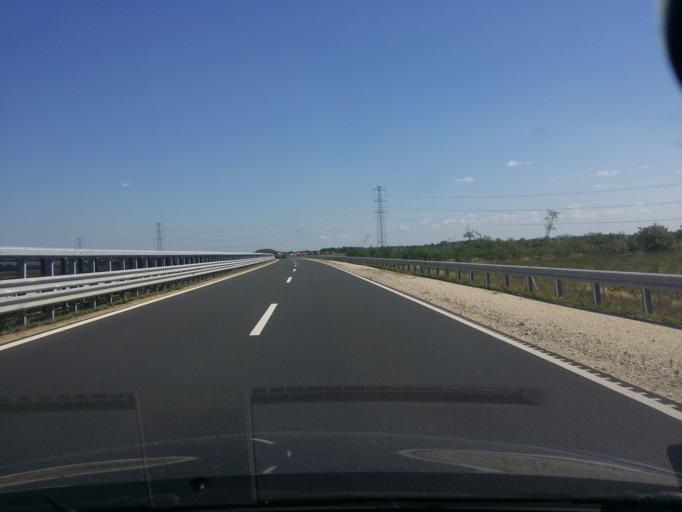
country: HU
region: Vas
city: Repcelak
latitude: 47.3913
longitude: 16.9912
